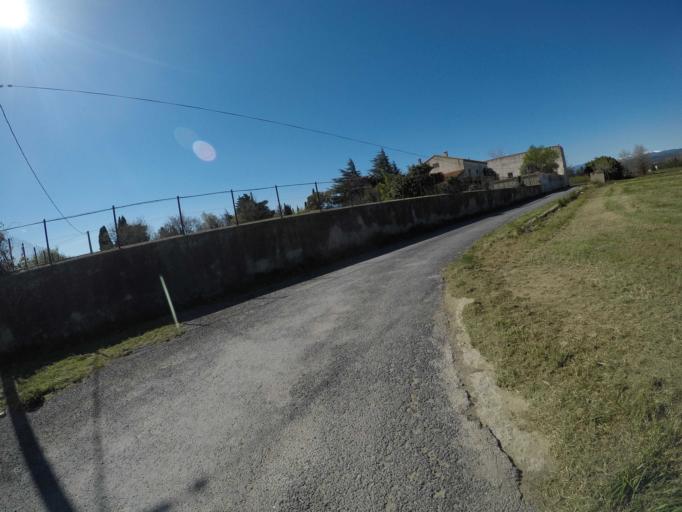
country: FR
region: Languedoc-Roussillon
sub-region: Departement des Pyrenees-Orientales
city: Ille-sur-Tet
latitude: 42.6853
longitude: 2.6558
